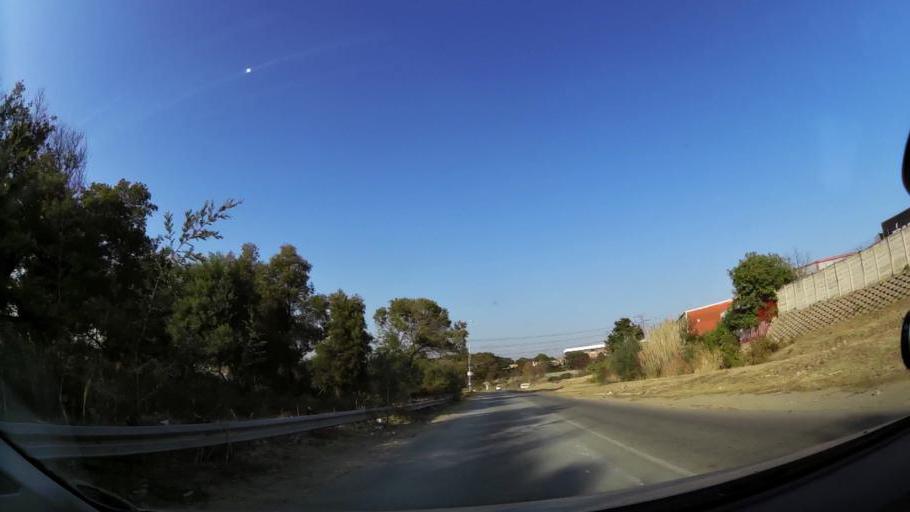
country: ZA
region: Gauteng
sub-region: City of Johannesburg Metropolitan Municipality
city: Modderfontein
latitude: -26.0868
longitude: 28.0903
